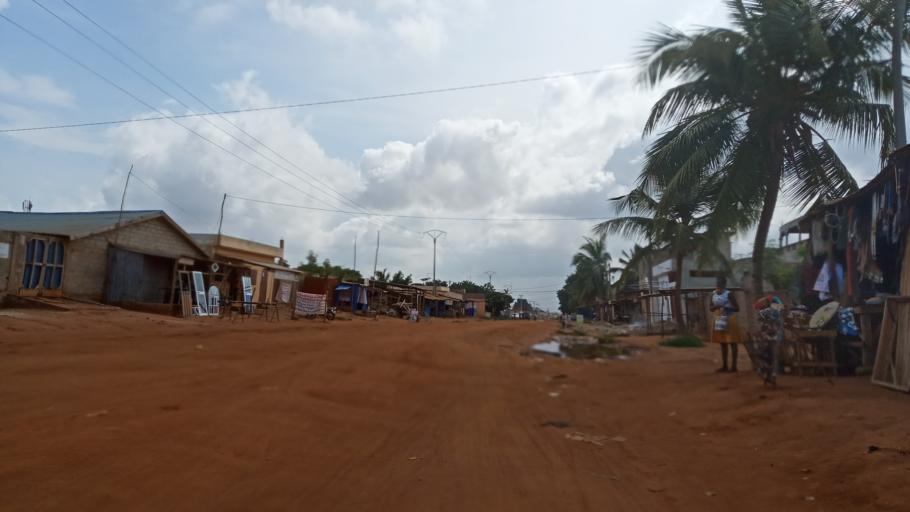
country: TG
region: Maritime
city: Lome
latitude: 6.2334
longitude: 1.1472
